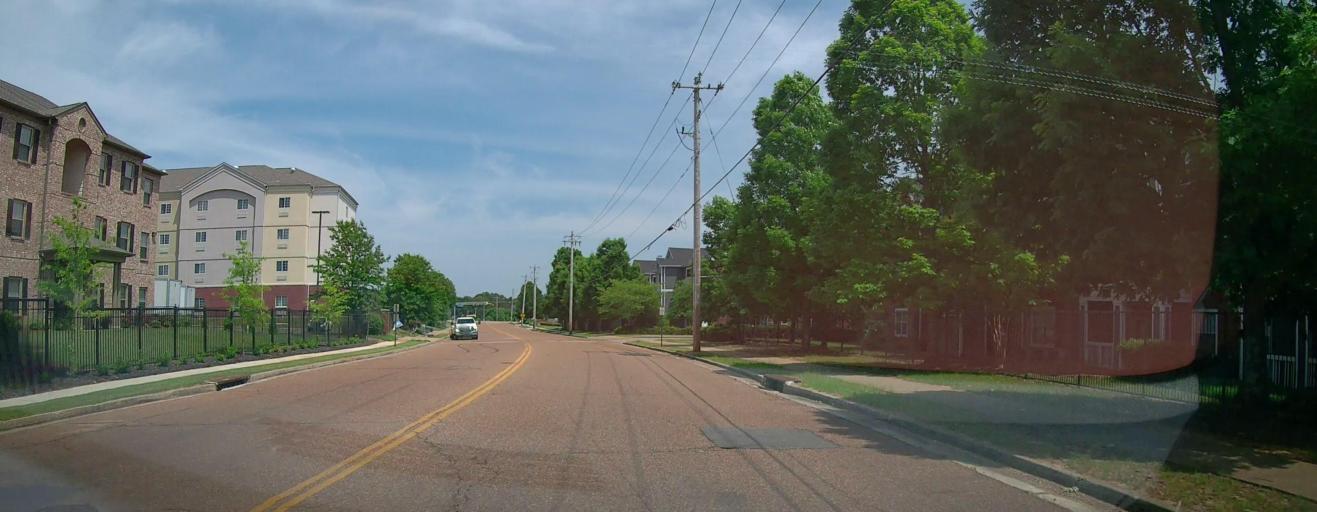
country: US
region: Tennessee
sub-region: Shelby County
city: Germantown
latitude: 35.0439
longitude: -89.7994
